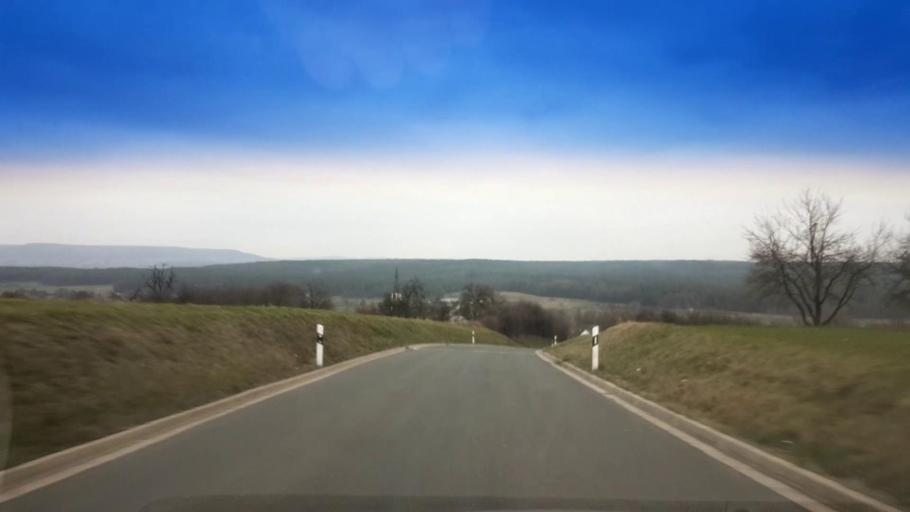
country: DE
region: Bavaria
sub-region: Upper Franconia
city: Hallerndorf
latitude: 49.7617
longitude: 10.9742
